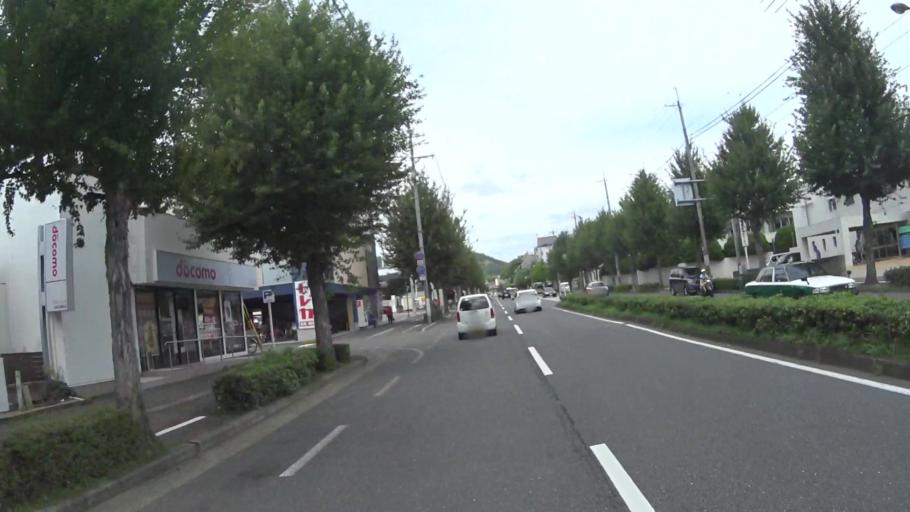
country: JP
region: Kyoto
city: Kyoto
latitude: 35.0285
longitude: 135.7314
